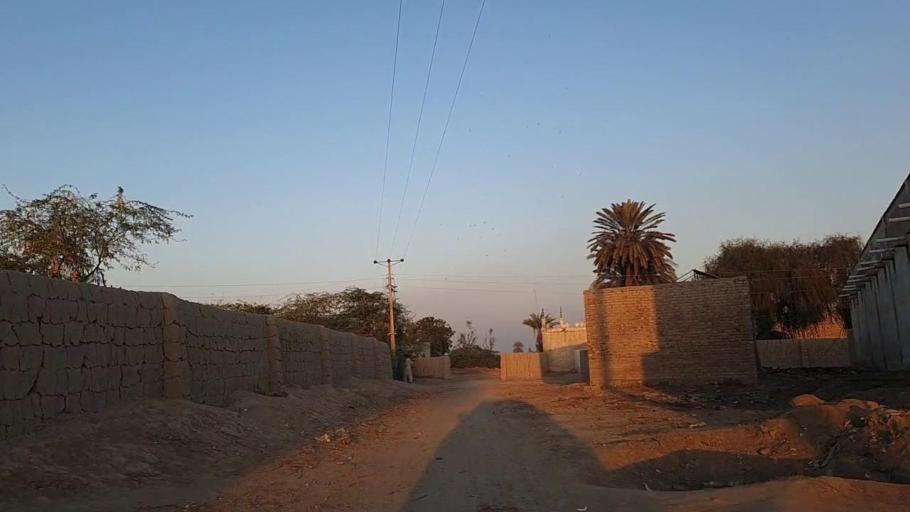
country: PK
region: Sindh
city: Jam Sahib
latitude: 26.3154
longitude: 68.6549
